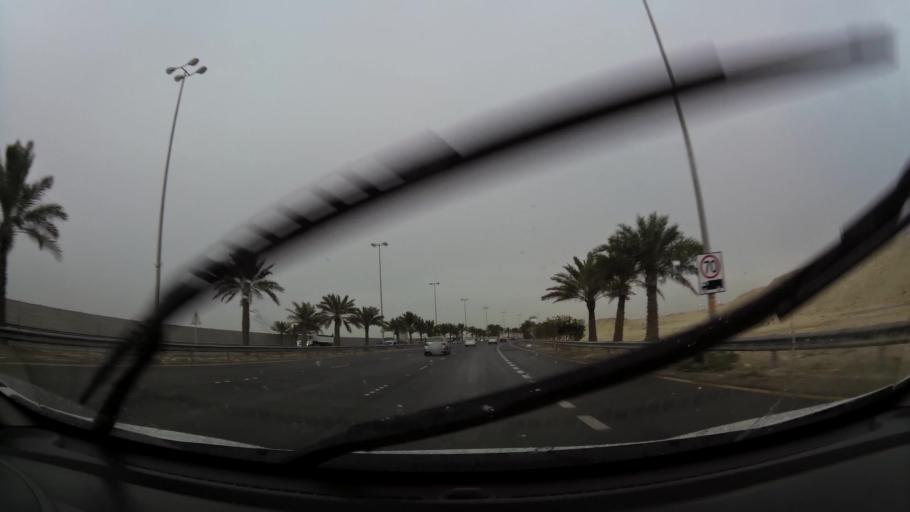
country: BH
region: Central Governorate
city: Madinat Hamad
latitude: 26.0921
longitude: 50.5145
